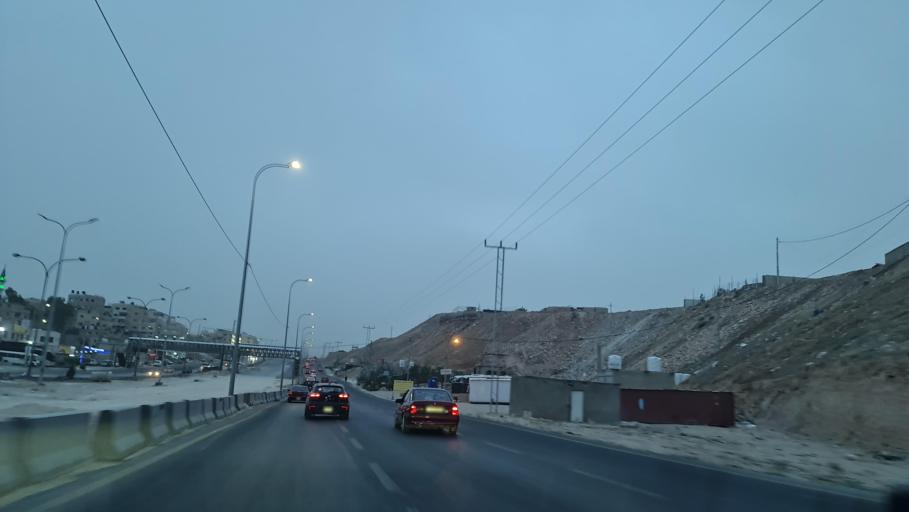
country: JO
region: Zarqa
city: Russeifa
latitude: 32.0119
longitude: 36.0551
